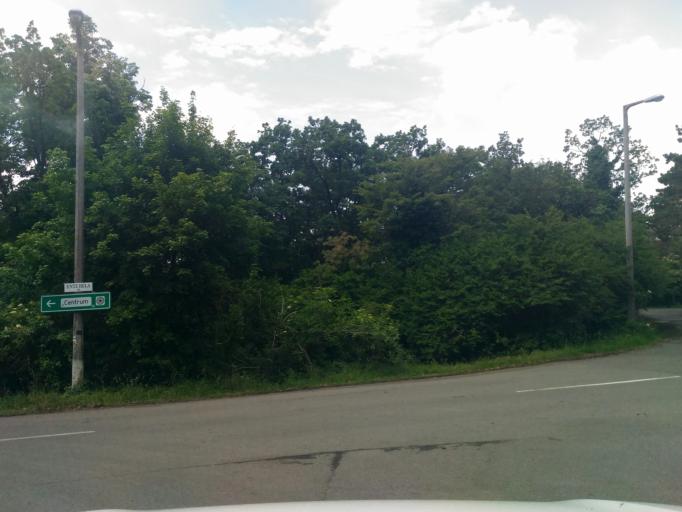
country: HU
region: Baranya
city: Pecs
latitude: 46.0989
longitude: 18.2167
